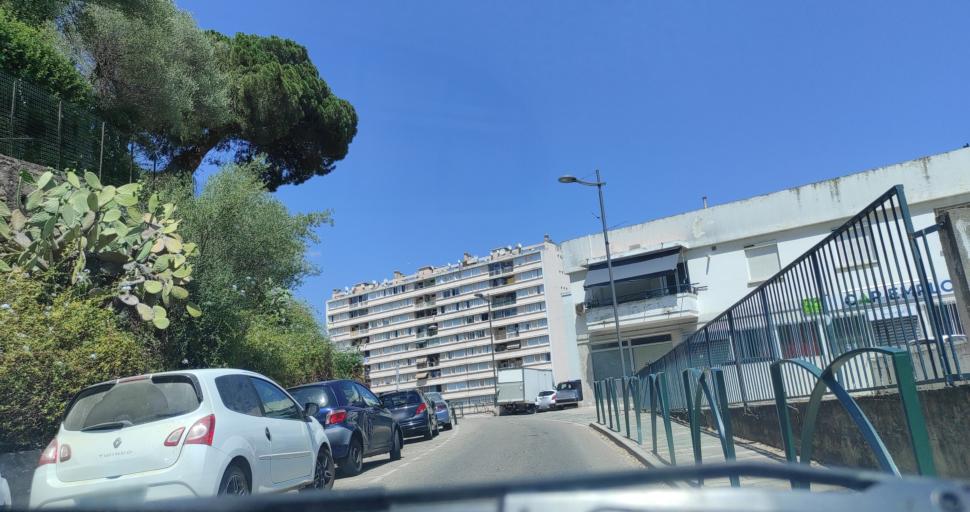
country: FR
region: Corsica
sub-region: Departement de la Corse-du-Sud
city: Ajaccio
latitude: 41.9336
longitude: 8.7407
